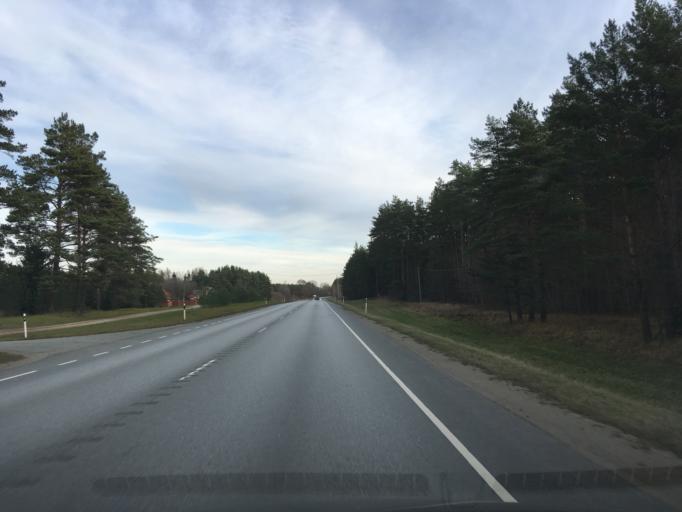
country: EE
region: Laeaene-Virumaa
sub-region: Viru-Nigula vald
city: Kunda
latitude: 59.4017
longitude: 26.6318
